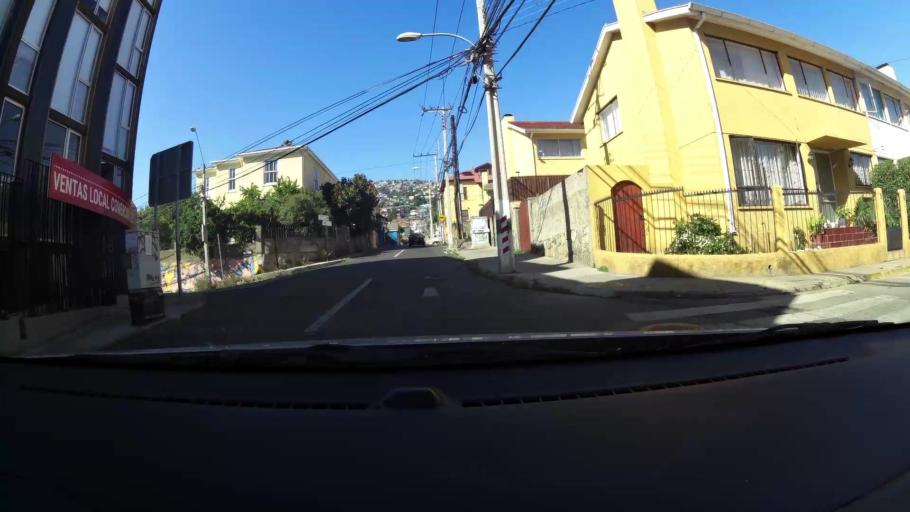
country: CL
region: Valparaiso
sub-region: Provincia de Valparaiso
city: Valparaiso
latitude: -33.0459
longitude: -71.6331
